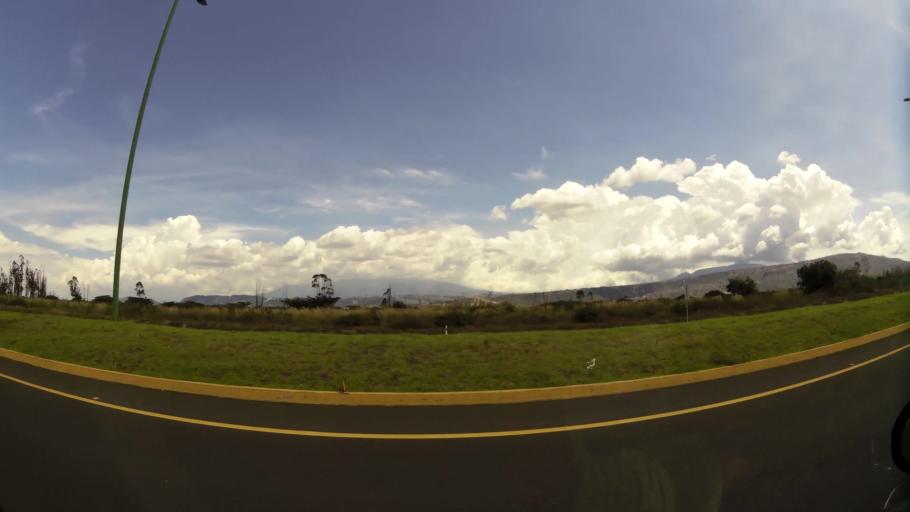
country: EC
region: Pichincha
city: Quito
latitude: -0.1209
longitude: -78.3652
